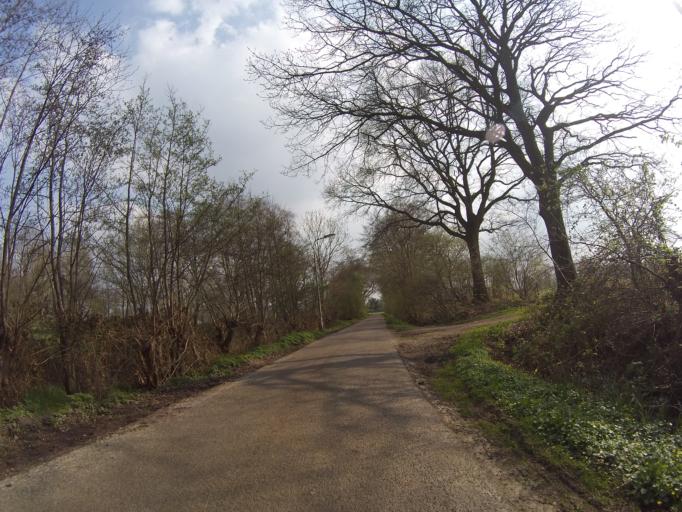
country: NL
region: Utrecht
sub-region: Gemeente Amersfoort
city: Hoogland
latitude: 52.1854
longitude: 5.3593
